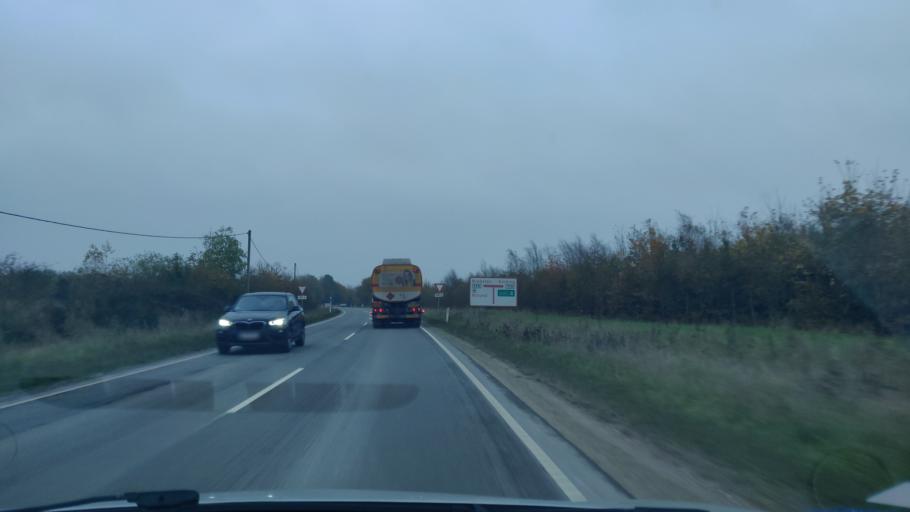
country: DK
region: South Denmark
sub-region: Kolding Kommune
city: Kolding
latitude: 55.5703
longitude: 9.4312
